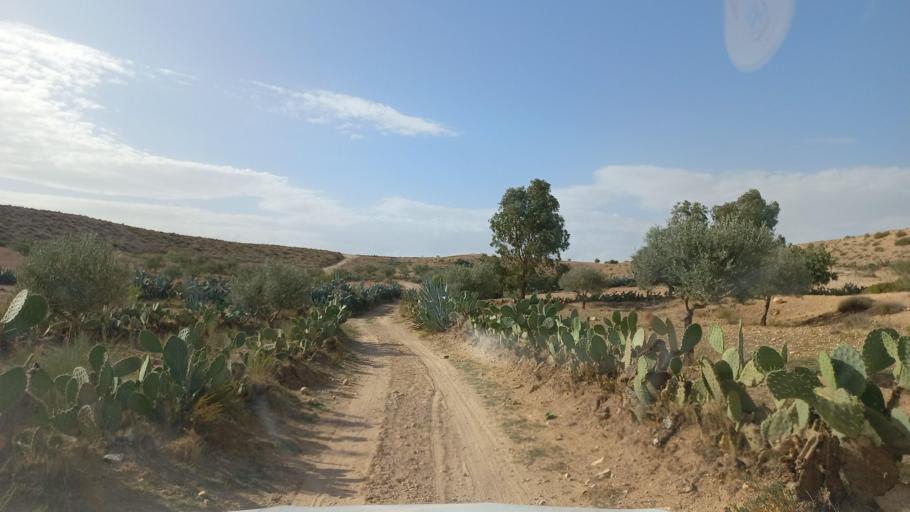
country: TN
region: Al Qasrayn
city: Kasserine
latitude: 35.2589
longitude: 8.9274
